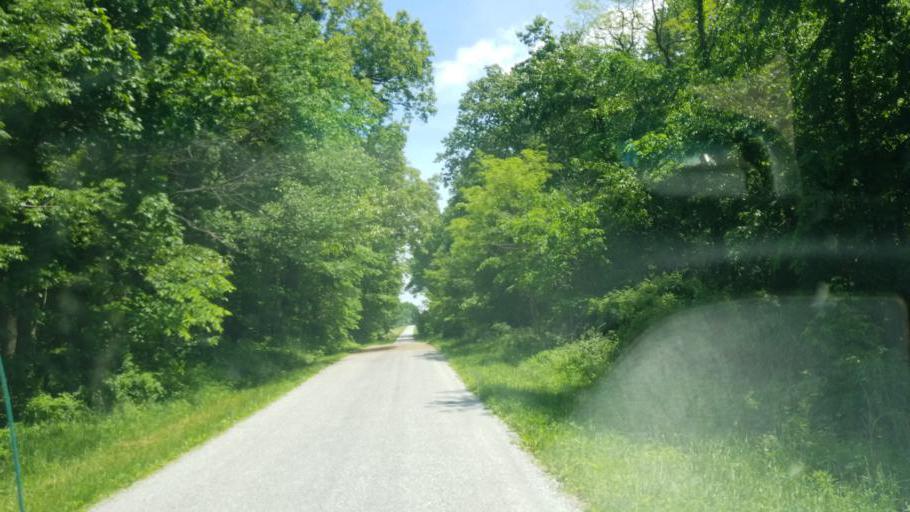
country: US
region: Ohio
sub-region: Wayne County
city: West Salem
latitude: 40.8425
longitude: -82.1737
